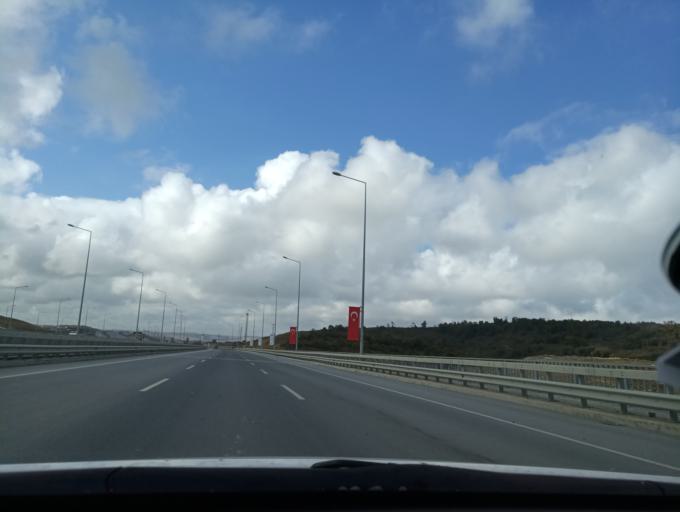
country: TR
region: Istanbul
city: Durusu
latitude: 41.2446
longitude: 28.7773
